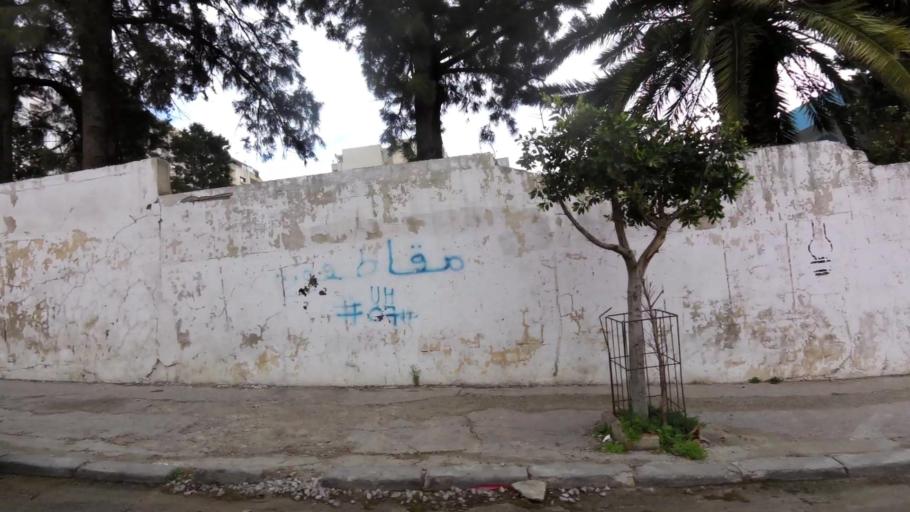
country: MA
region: Tanger-Tetouan
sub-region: Tanger-Assilah
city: Tangier
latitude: 35.7710
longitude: -5.8169
